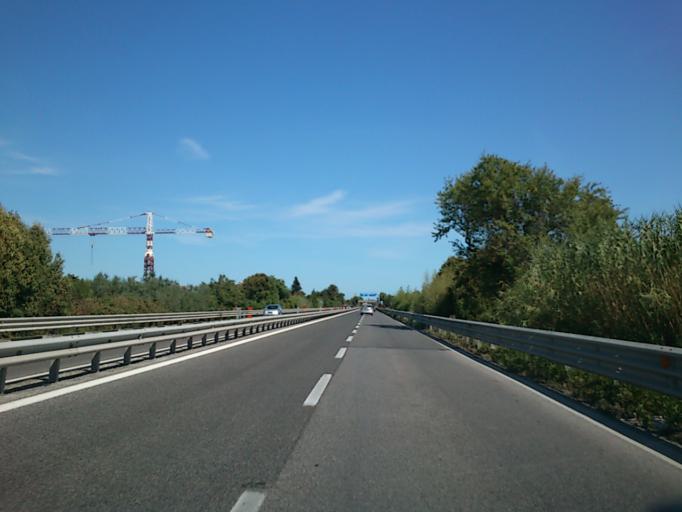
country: IT
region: The Marches
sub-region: Provincia di Pesaro e Urbino
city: Bellocchi
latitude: 43.7841
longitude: 12.9912
